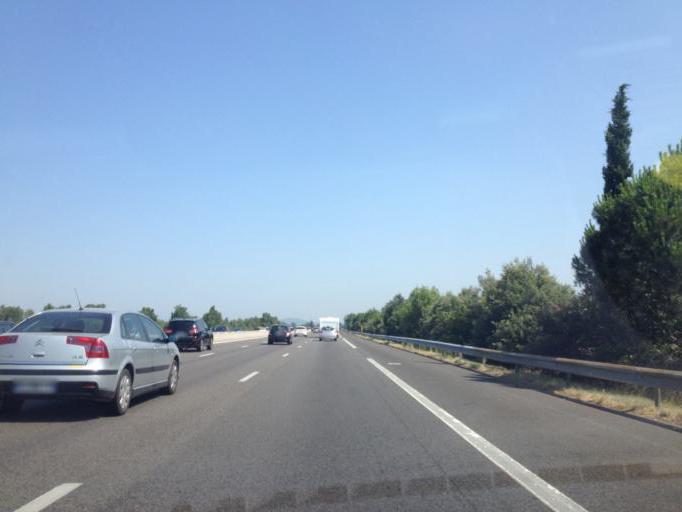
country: FR
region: Rhone-Alpes
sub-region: Departement de la Drome
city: Saint-Paul-Trois-Chateaux
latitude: 44.3417
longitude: 4.7380
